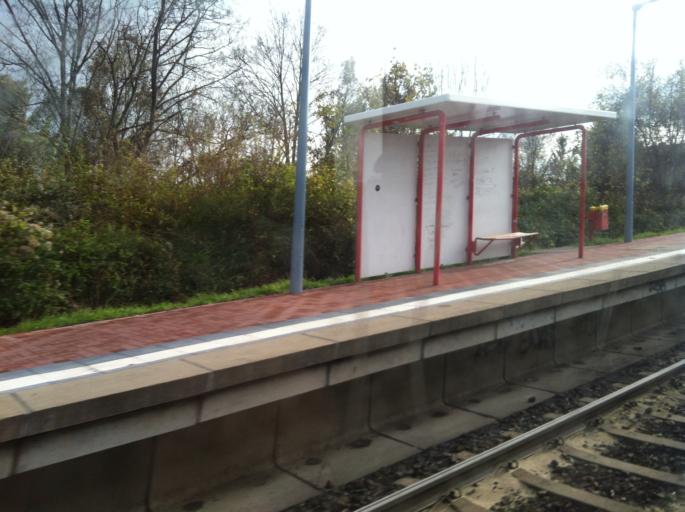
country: DE
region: North Rhine-Westphalia
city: Wesseling
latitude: 50.8318
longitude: 6.9711
